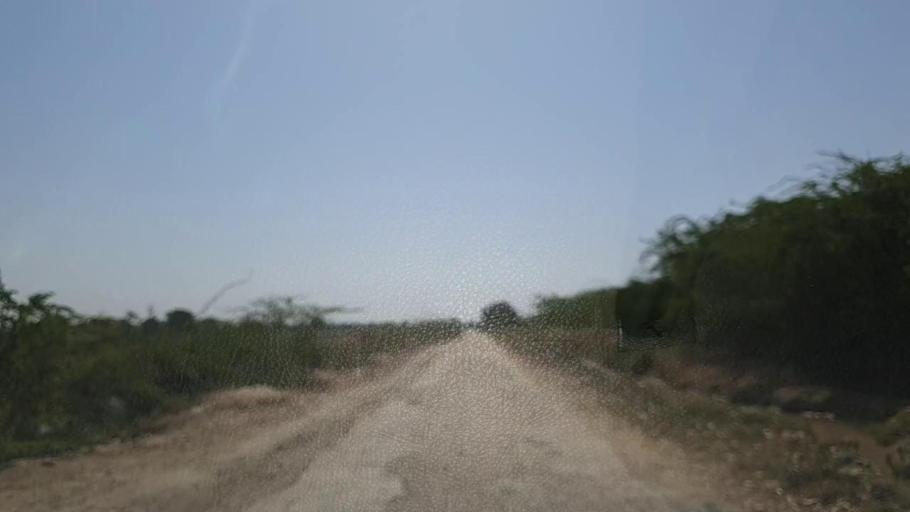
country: PK
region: Sindh
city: Samaro
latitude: 25.2496
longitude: 69.4100
